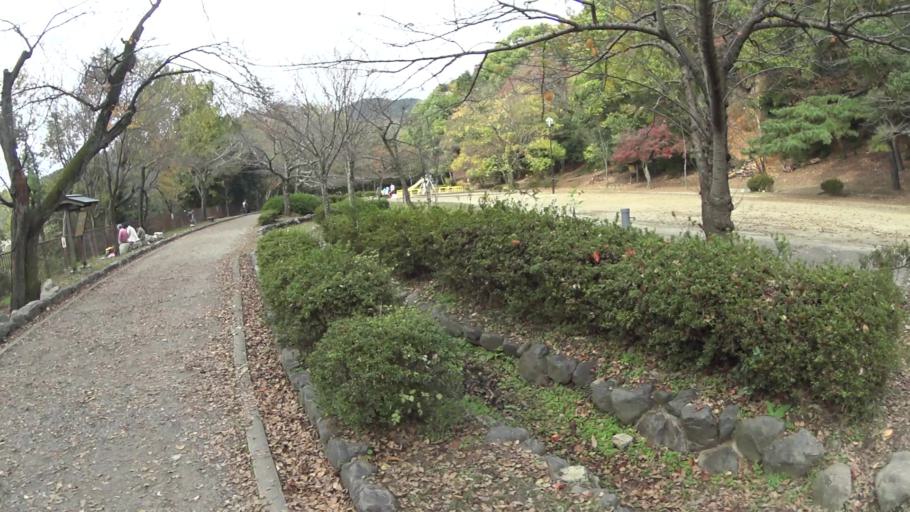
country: JP
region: Shiga Prefecture
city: Otsu-shi
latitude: 34.9932
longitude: 135.8224
